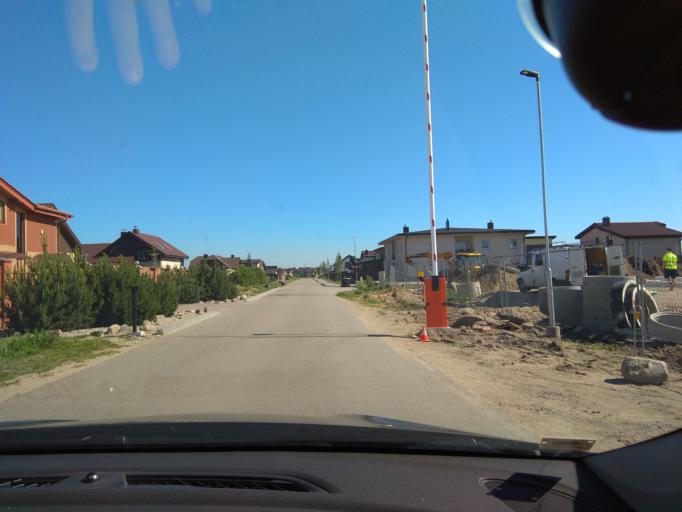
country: LT
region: Klaipedos apskritis
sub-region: Klaipeda
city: Klaipeda
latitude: 55.7525
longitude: 21.1760
